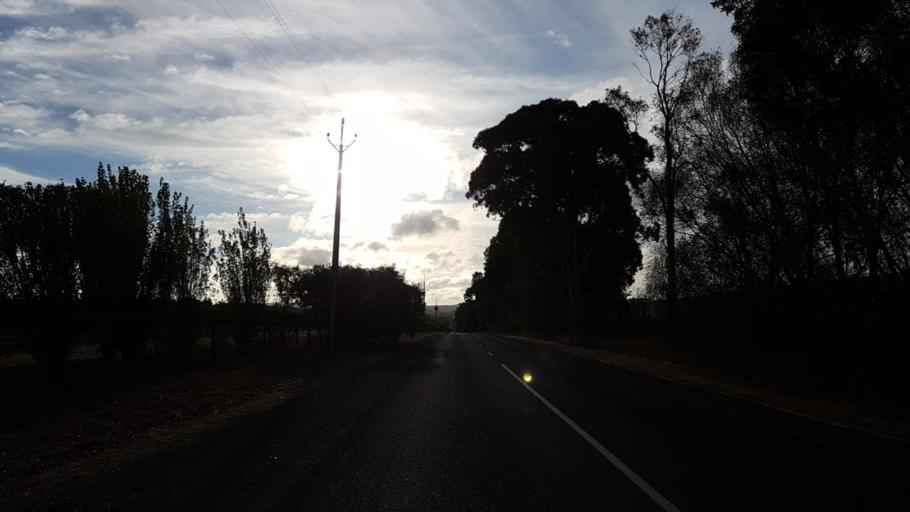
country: AU
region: South Australia
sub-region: Adelaide Hills
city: Woodside
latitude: -34.9782
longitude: 138.8795
